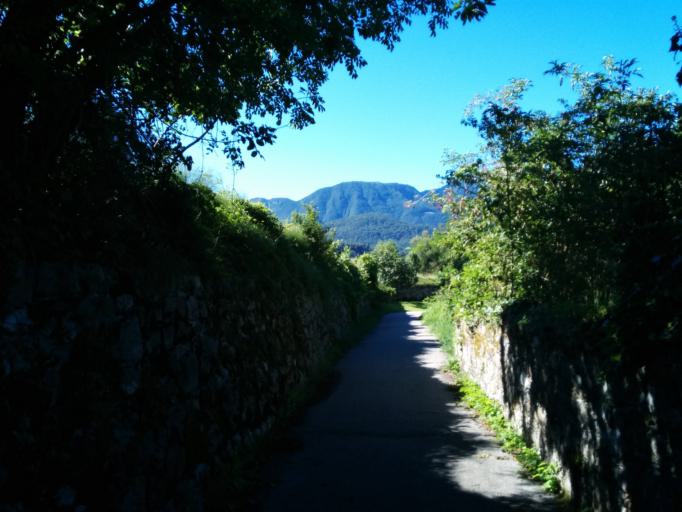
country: IT
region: Friuli Venezia Giulia
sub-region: Provincia di Udine
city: Tolmezzo
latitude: 46.4084
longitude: 13.0031
